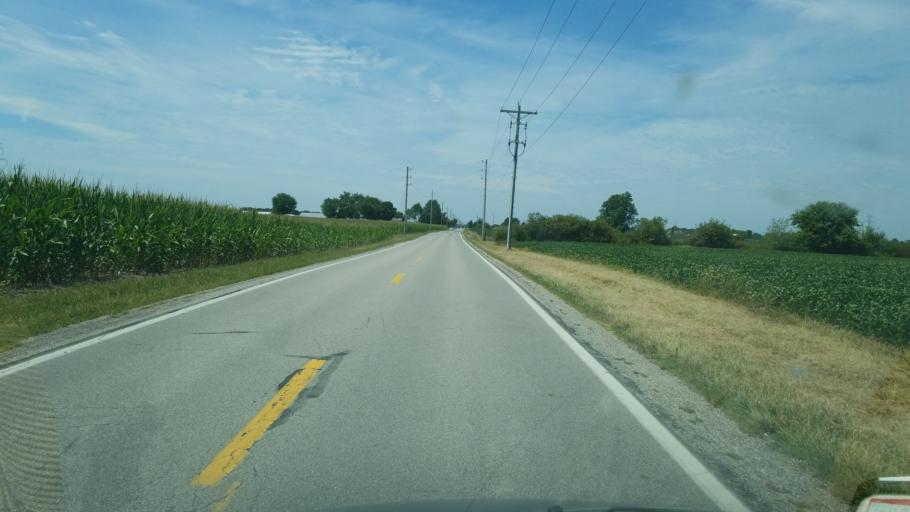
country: US
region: Ohio
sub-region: Franklin County
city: Grove City
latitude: 39.8600
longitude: -83.1206
